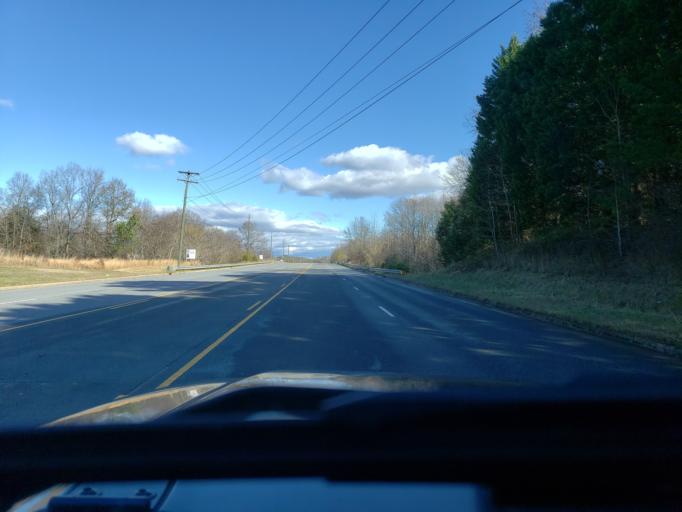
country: US
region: North Carolina
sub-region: Cleveland County
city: Shelby
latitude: 35.2619
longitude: -81.5536
